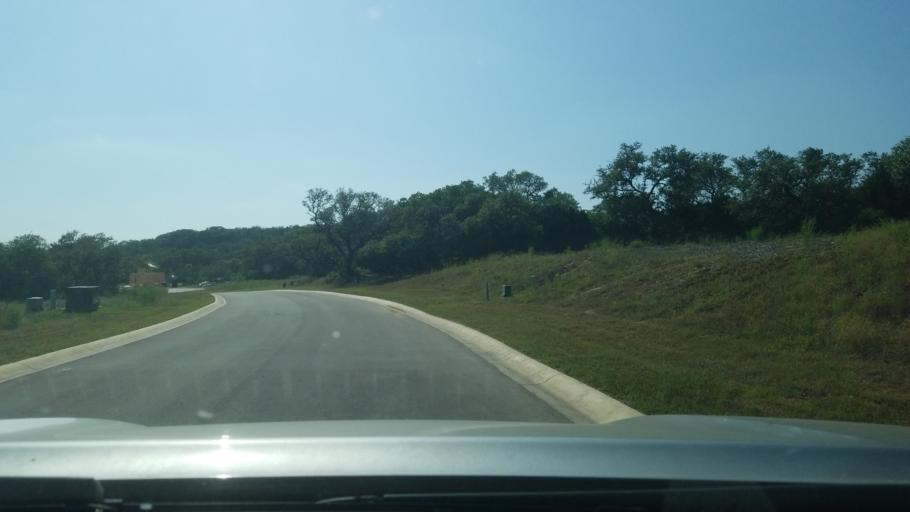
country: US
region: Texas
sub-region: Comal County
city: Bulverde
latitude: 29.7630
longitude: -98.4182
